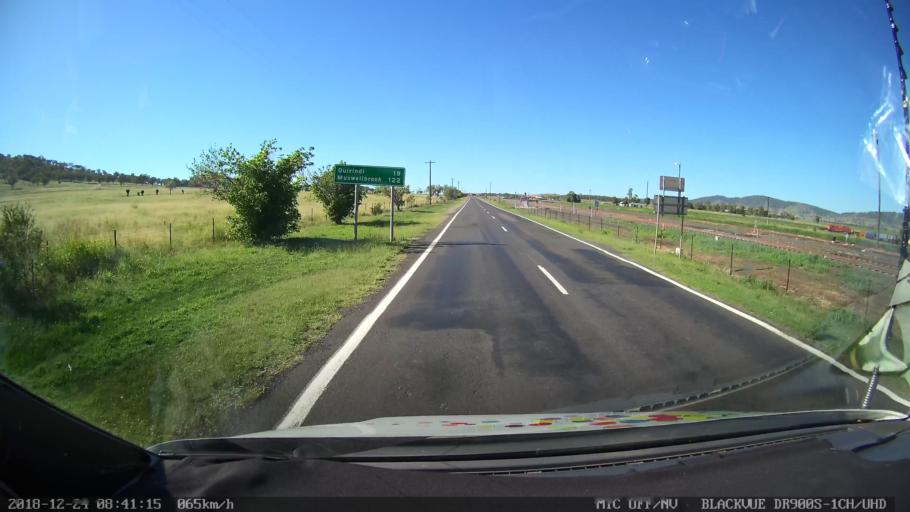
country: AU
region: New South Wales
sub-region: Liverpool Plains
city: Quirindi
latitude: -31.3613
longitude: 150.6452
